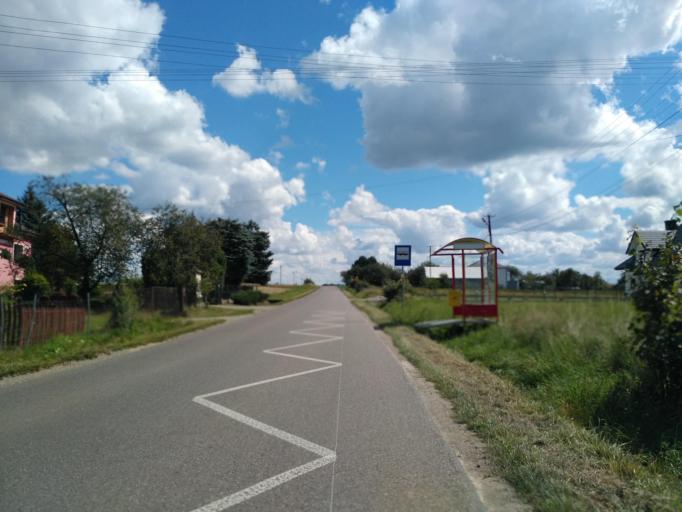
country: PL
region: Subcarpathian Voivodeship
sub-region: Powiat jasielski
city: Trzcinica
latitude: 49.7516
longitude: 21.4268
